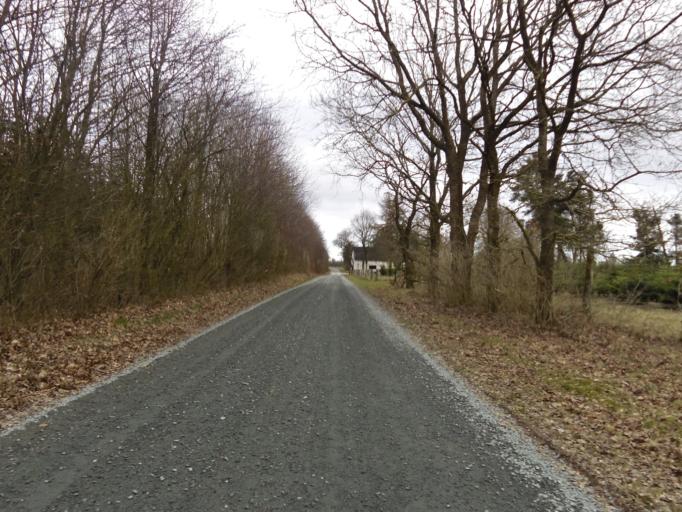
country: DK
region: South Denmark
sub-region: Tonder Kommune
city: Toftlund
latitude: 55.2137
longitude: 9.1640
